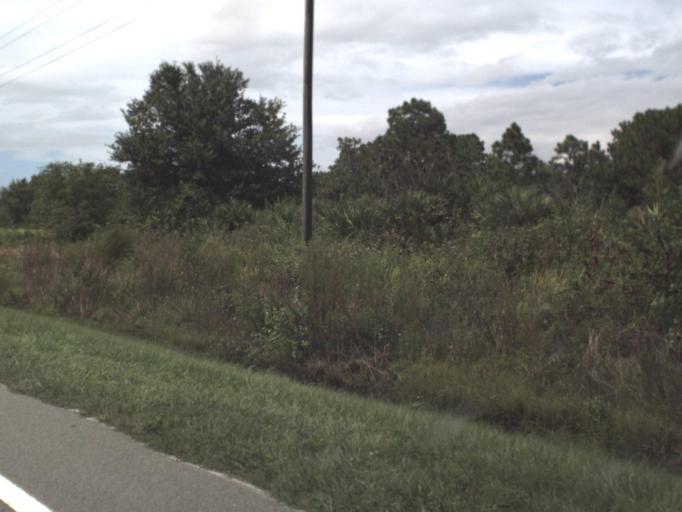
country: US
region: Florida
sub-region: Hillsborough County
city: Wimauma
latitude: 27.5947
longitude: -82.2692
